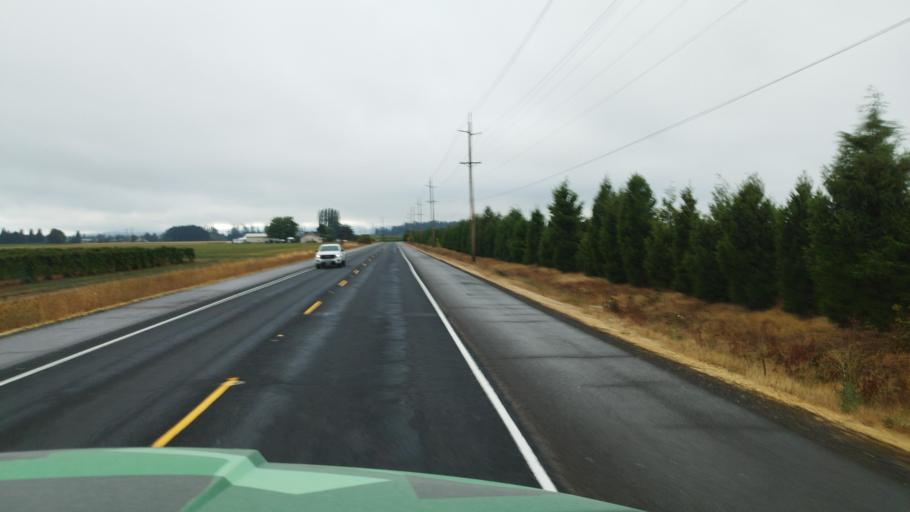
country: US
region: Oregon
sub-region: Washington County
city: Cornelius
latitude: 45.5456
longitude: -123.0734
